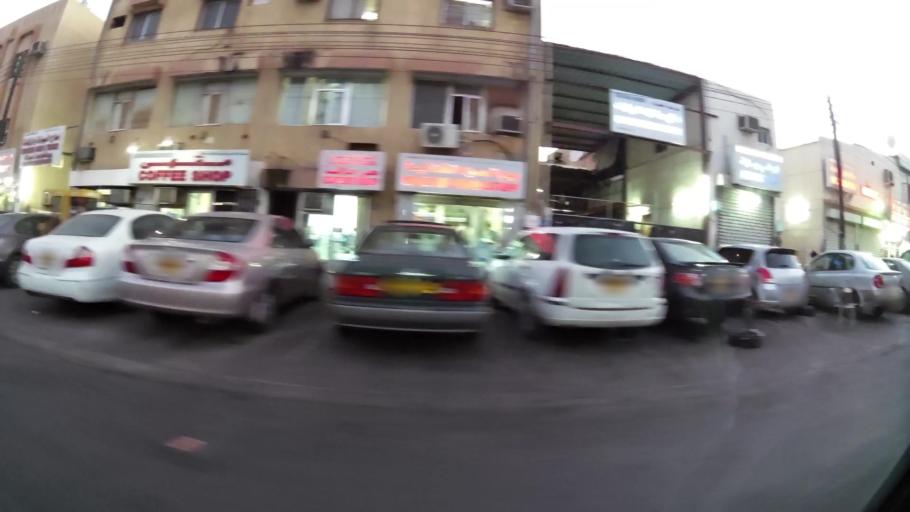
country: OM
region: Muhafazat Masqat
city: Muscat
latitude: 23.5944
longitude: 58.5604
